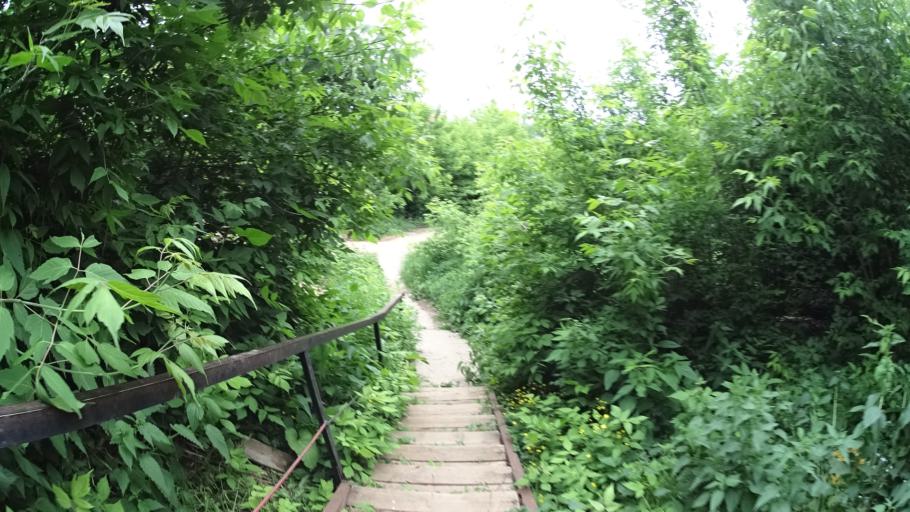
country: RU
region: Perm
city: Perm
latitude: 58.0201
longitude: 56.2653
